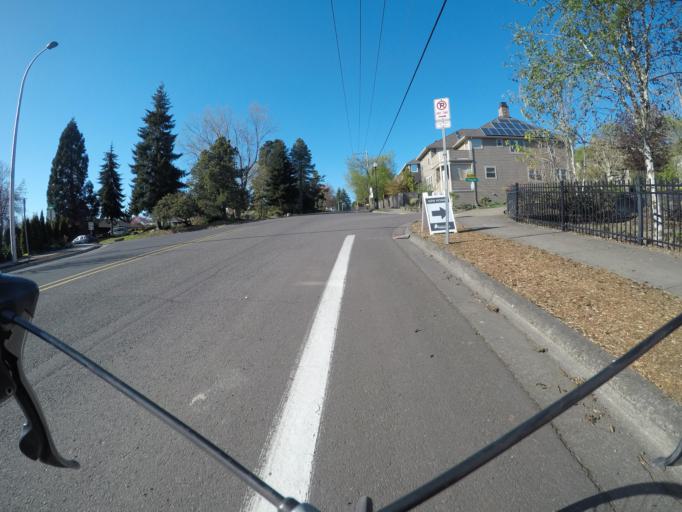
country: US
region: Oregon
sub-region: Washington County
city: King City
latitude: 45.4124
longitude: -122.8313
